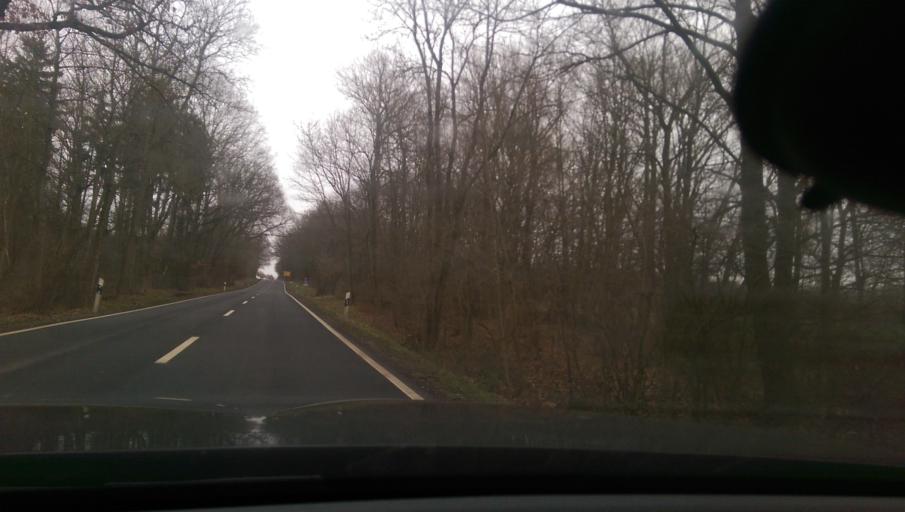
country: DE
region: Hesse
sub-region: Regierungsbezirk Kassel
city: Kaufungen
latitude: 51.3089
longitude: 9.6076
